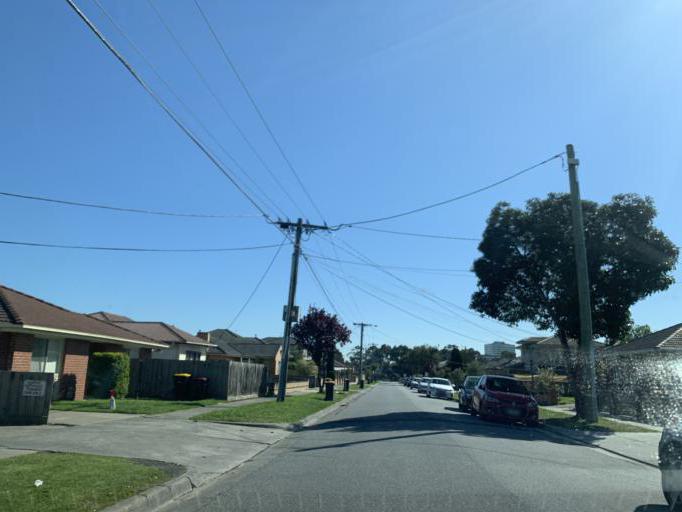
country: AU
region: Victoria
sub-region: Greater Dandenong
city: Dandenong
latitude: -37.9958
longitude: 145.2078
